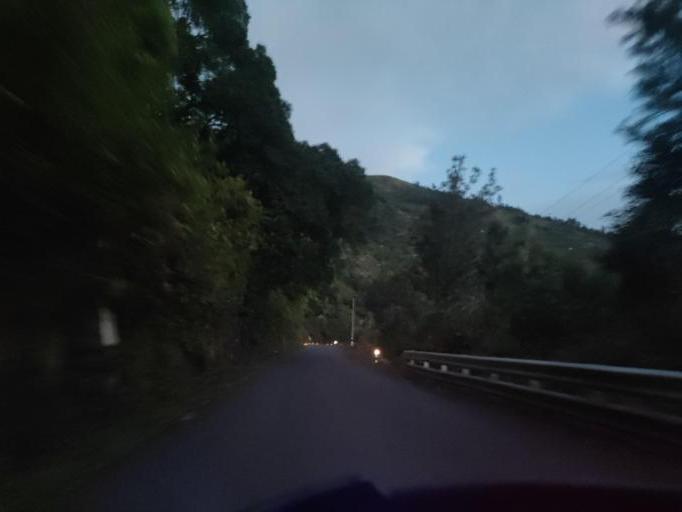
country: IN
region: Tamil Nadu
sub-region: Dindigul
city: Kodaikanal
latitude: 10.2891
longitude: 77.5375
